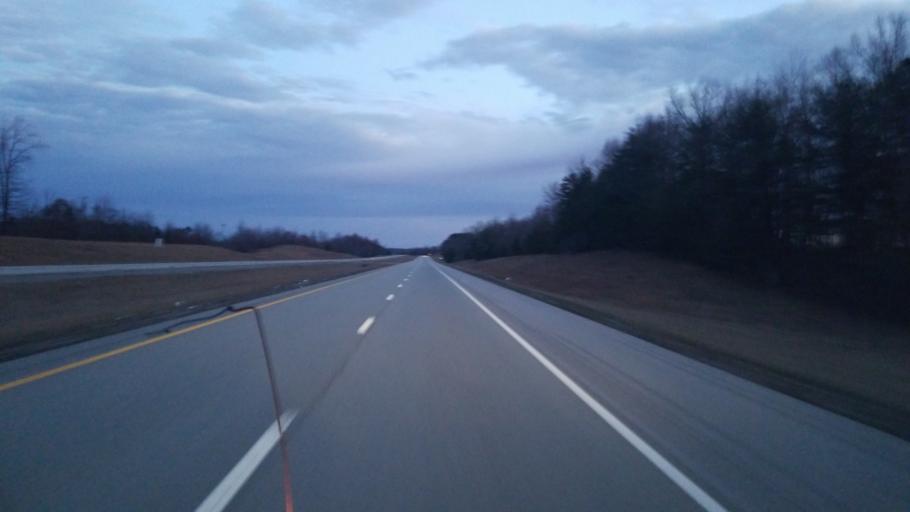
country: US
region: Tennessee
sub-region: Van Buren County
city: Spencer
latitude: 35.6620
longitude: -85.4739
